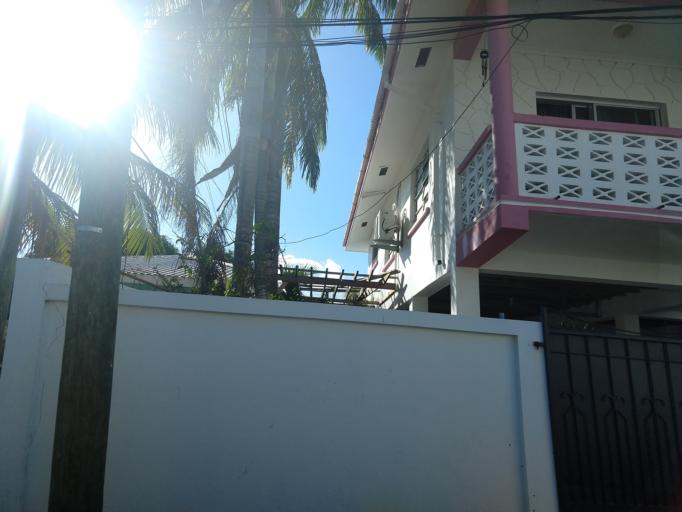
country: BZ
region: Belize
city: Belize City
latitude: 17.4972
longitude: -88.1836
